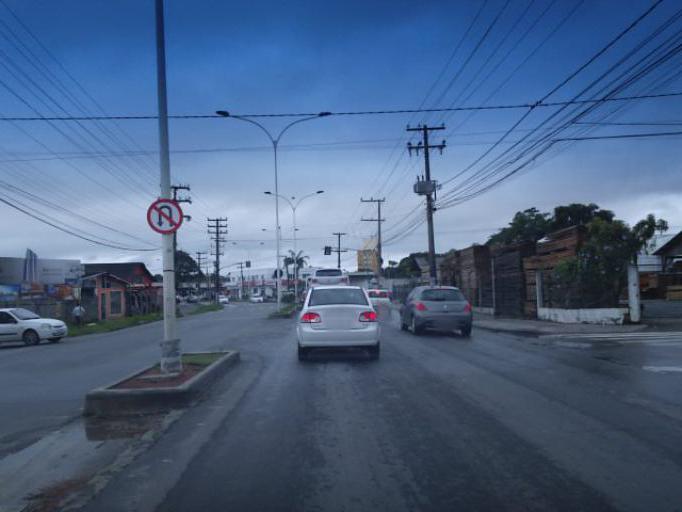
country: BR
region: Santa Catarina
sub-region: Itajai
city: Itajai
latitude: -26.8879
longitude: -48.7009
